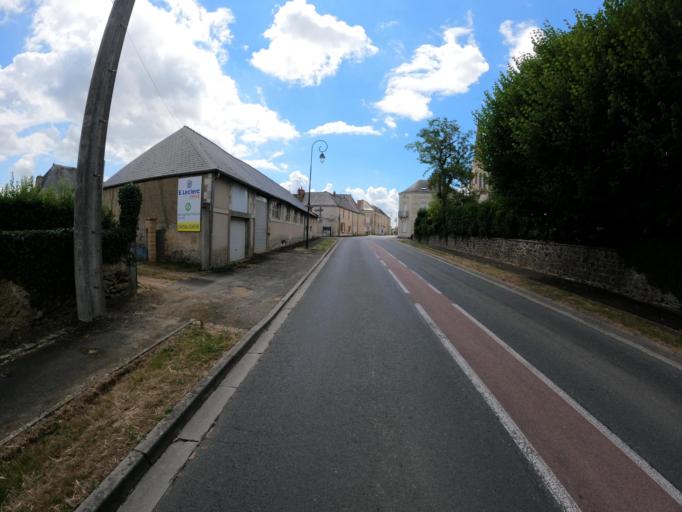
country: FR
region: Pays de la Loire
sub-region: Departement de Maine-et-Loire
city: Mire
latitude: 47.7305
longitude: -0.5162
